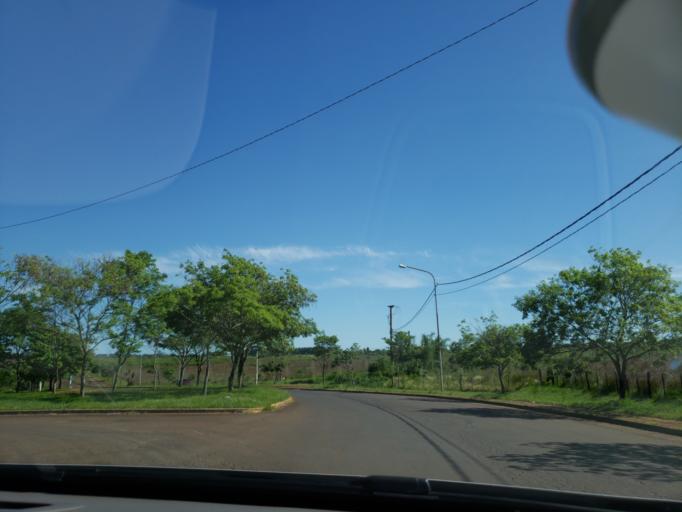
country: AR
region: Misiones
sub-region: Departamento de Capital
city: Posadas
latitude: -27.3824
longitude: -55.9633
